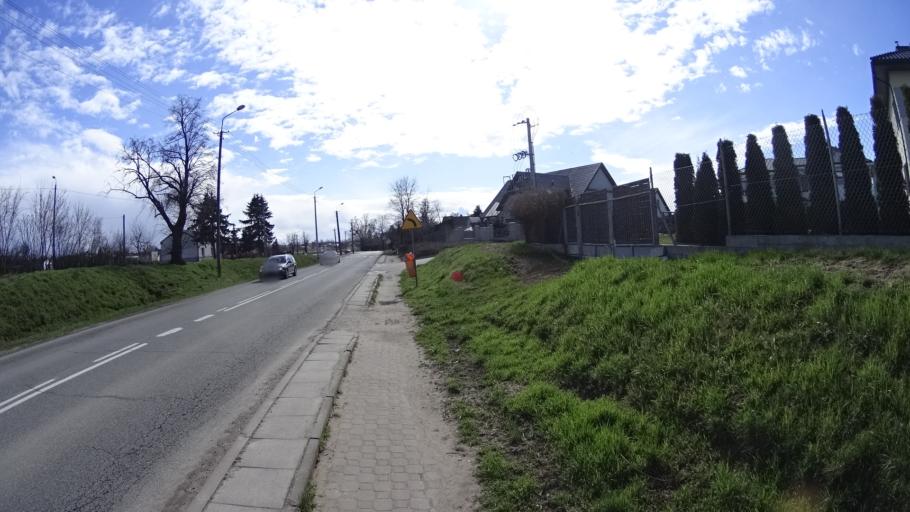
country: PL
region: Masovian Voivodeship
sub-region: Powiat warszawski zachodni
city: Jozefow
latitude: 52.2058
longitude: 20.6966
